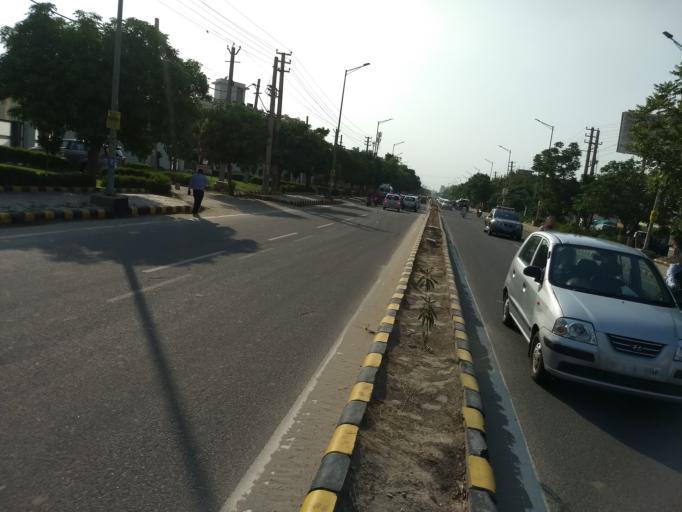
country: IN
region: Haryana
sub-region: Gurgaon
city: Gurgaon
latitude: 28.4330
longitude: 77.0722
